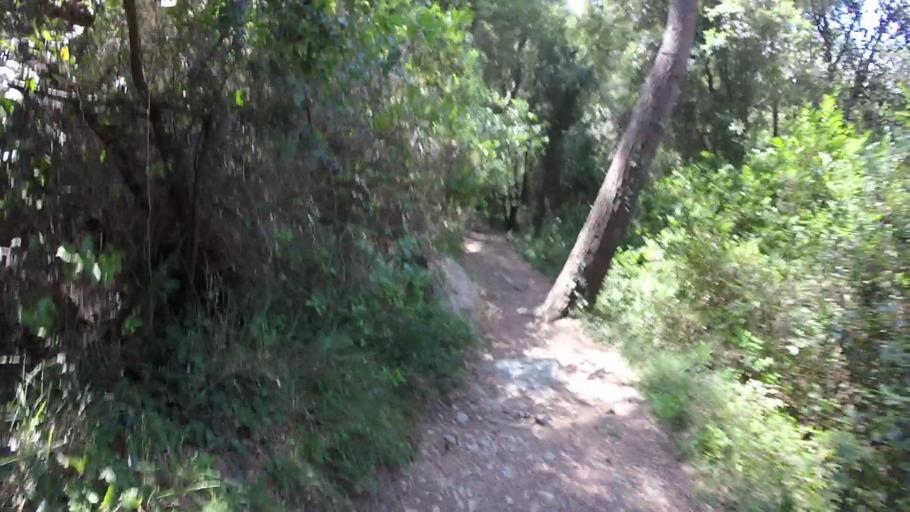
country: FR
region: Provence-Alpes-Cote d'Azur
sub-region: Departement des Alpes-Maritimes
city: Mougins
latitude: 43.5989
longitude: 7.0251
